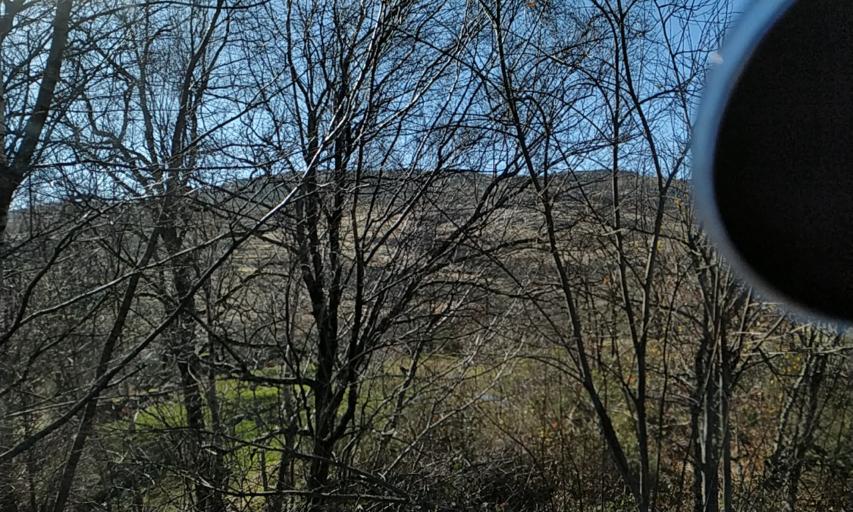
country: PT
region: Vila Real
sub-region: Vila Real
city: Vila Real
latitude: 41.3790
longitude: -7.8137
